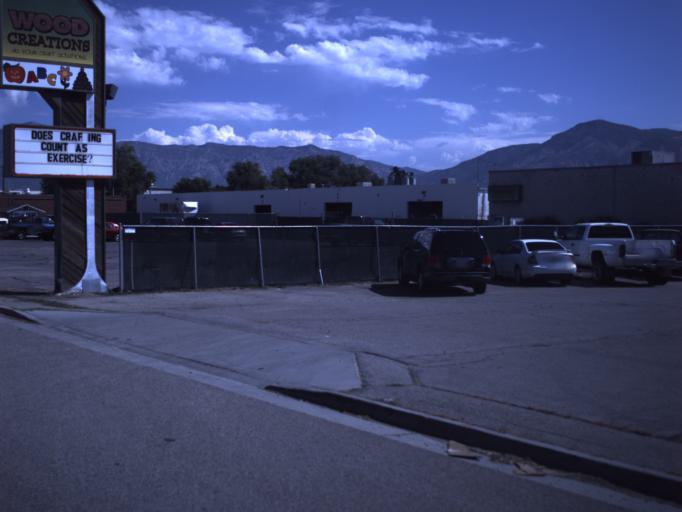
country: US
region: Utah
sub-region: Weber County
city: Marriott-Slaterville
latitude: 41.2217
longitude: -112.0256
